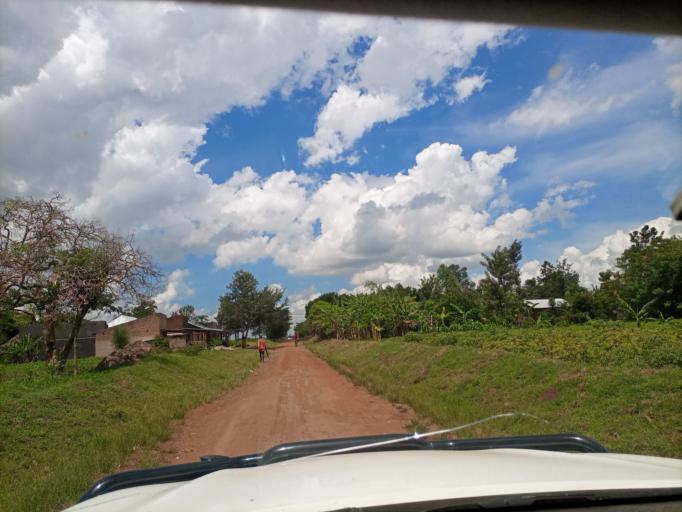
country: UG
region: Eastern Region
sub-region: Busia District
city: Busia
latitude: 0.6322
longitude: 33.9916
